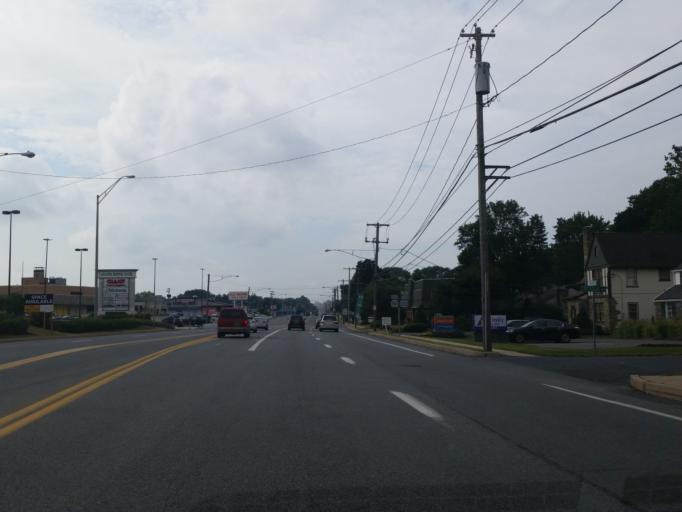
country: US
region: Pennsylvania
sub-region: Lancaster County
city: Lancaster
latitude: 40.0677
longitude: -76.3074
